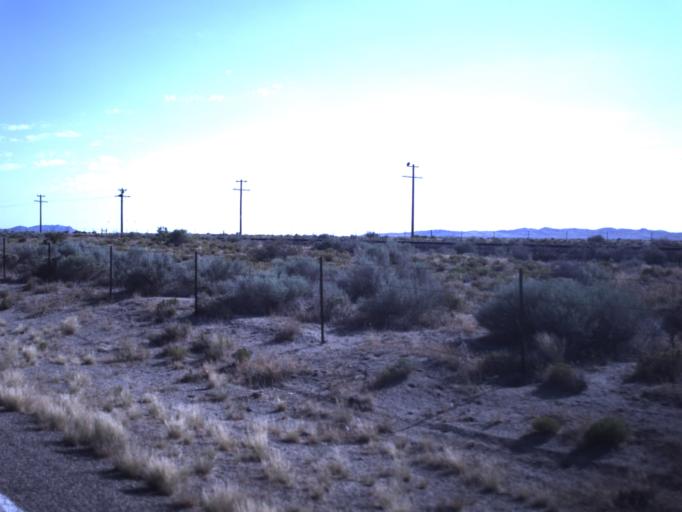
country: US
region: Utah
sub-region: Beaver County
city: Milford
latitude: 38.6588
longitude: -112.9817
